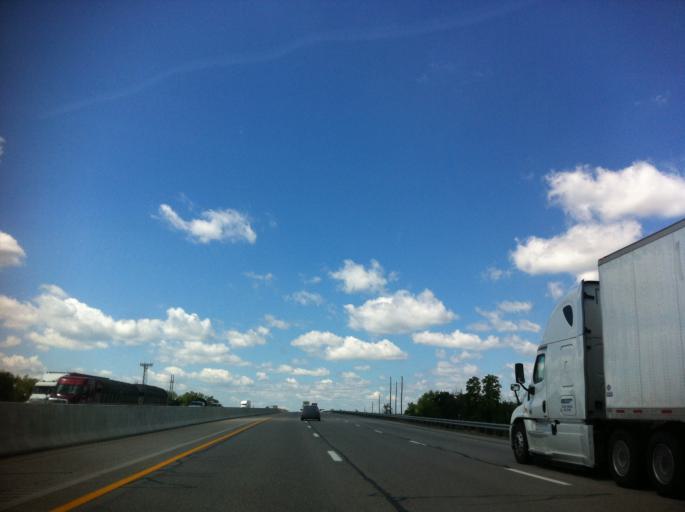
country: US
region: Ohio
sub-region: Wood County
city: Walbridge
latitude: 41.5315
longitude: -83.4777
